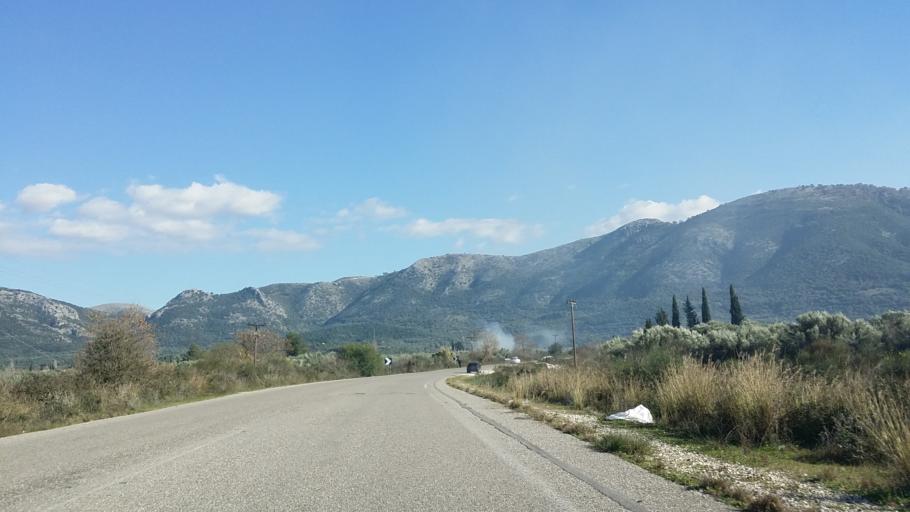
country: GR
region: West Greece
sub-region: Nomos Aitolias kai Akarnanias
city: Kandila
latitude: 38.6777
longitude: 20.9733
